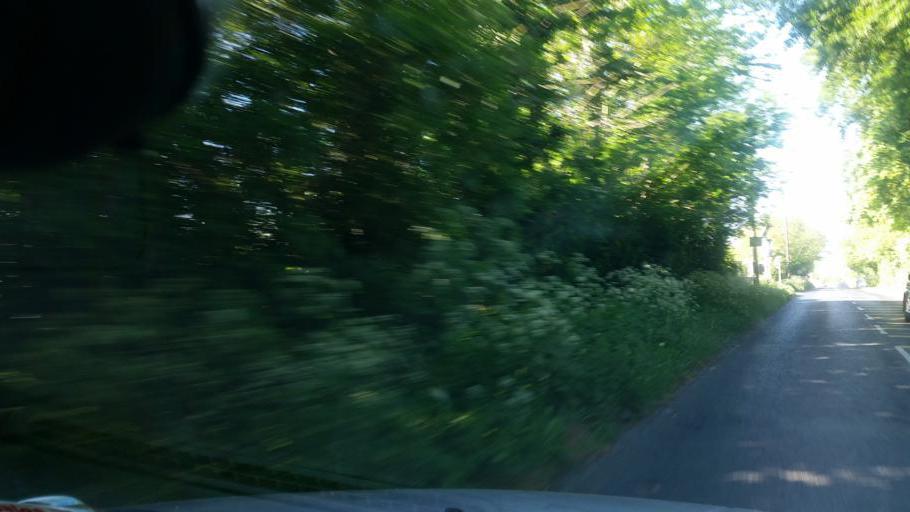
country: IE
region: Leinster
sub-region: Fingal County
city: Blanchardstown
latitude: 53.4095
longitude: -6.3906
